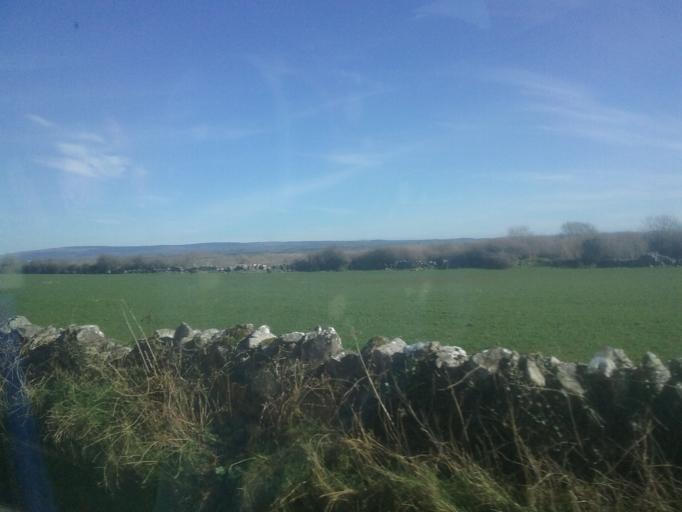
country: IE
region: Munster
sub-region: An Clar
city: Ennis
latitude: 52.9878
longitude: -8.9904
